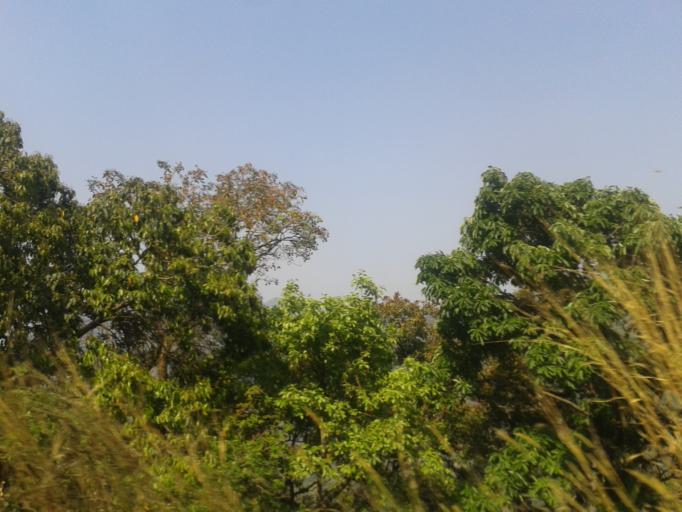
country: IN
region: Tamil Nadu
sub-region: Dindigul
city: Ayakudi
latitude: 10.3467
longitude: 77.5746
